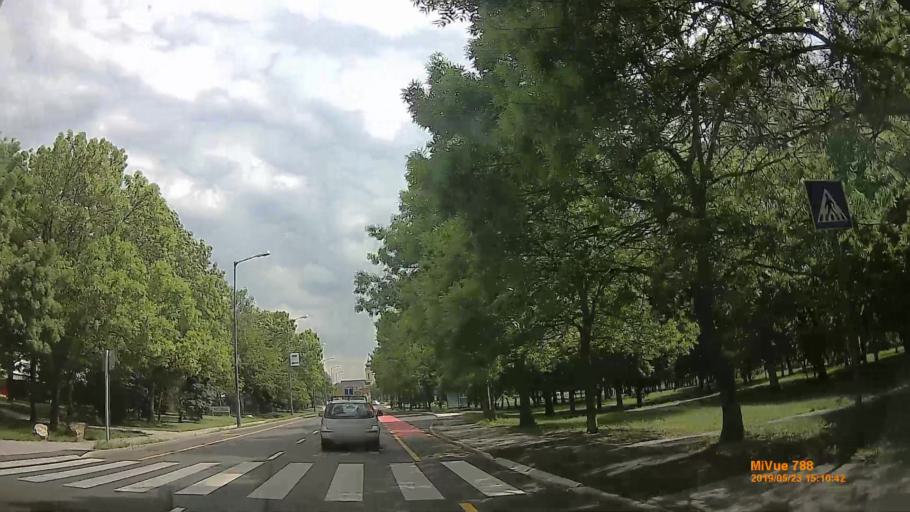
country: HU
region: Veszprem
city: Veszprem
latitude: 47.1042
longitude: 17.9122
